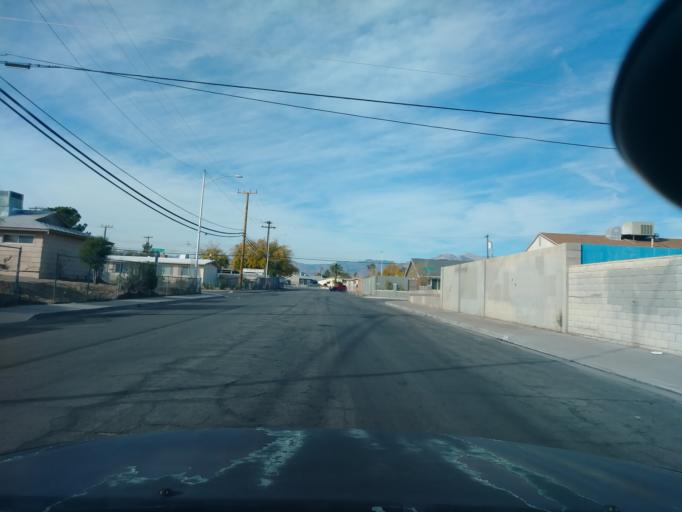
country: US
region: Nevada
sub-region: Clark County
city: Spring Valley
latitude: 36.1632
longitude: -115.2266
